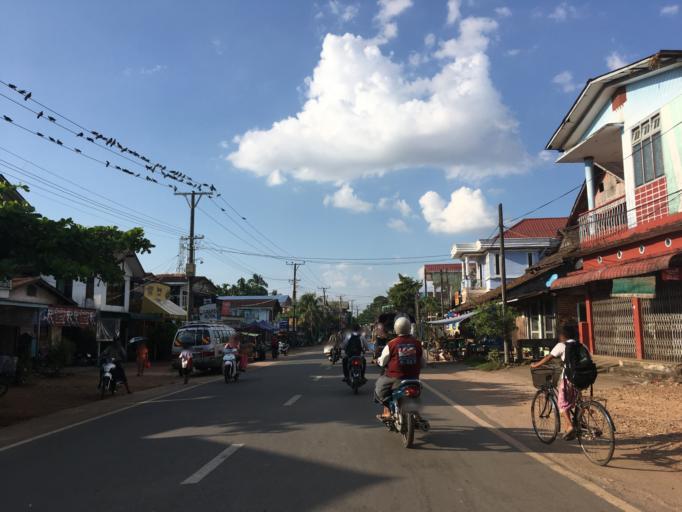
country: MM
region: Mon
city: Mawlamyine
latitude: 16.4573
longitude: 97.6266
